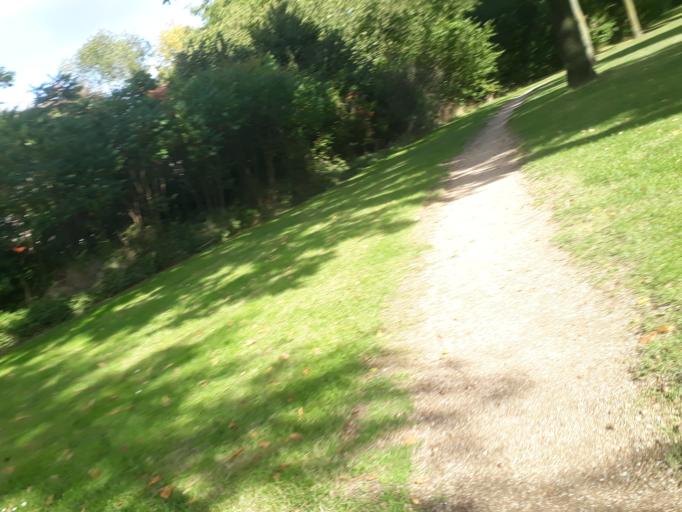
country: NL
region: Gelderland
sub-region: Gemeente Zevenaar
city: Zevenaar
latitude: 51.9344
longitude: 6.0519
